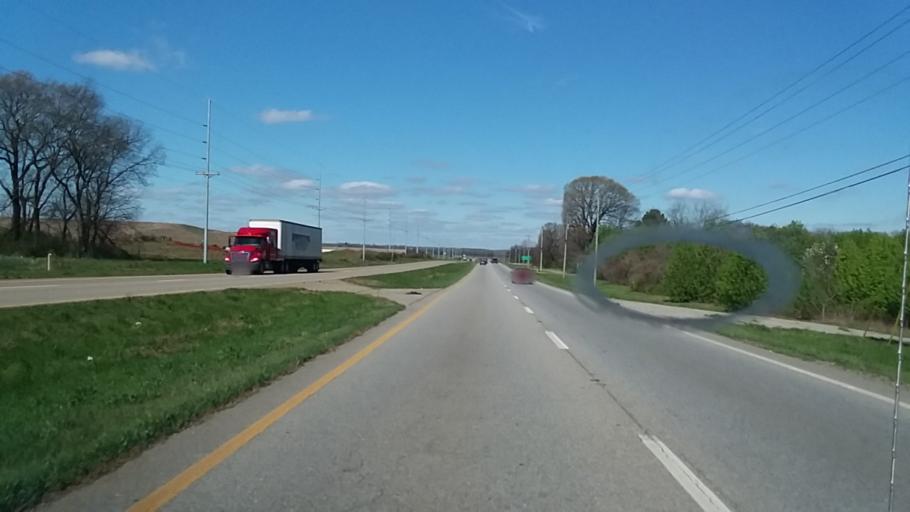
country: US
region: Alabama
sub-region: Morgan County
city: Trinity
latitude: 34.6281
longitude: -87.0907
